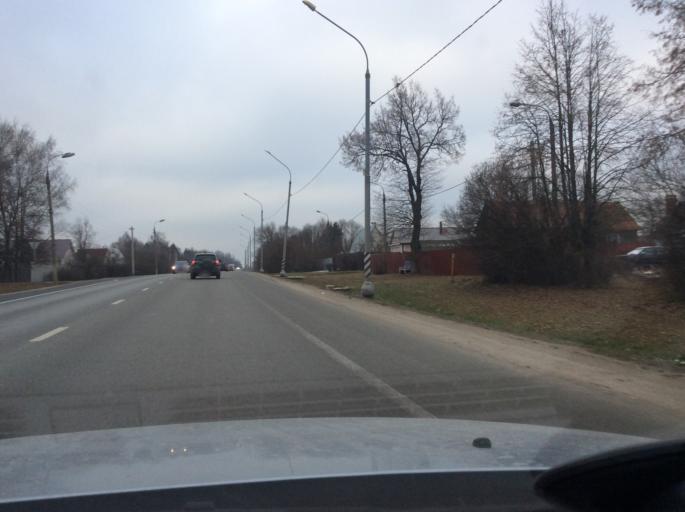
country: RU
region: Moskovskaya
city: Troitsk
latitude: 55.3693
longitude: 37.2010
